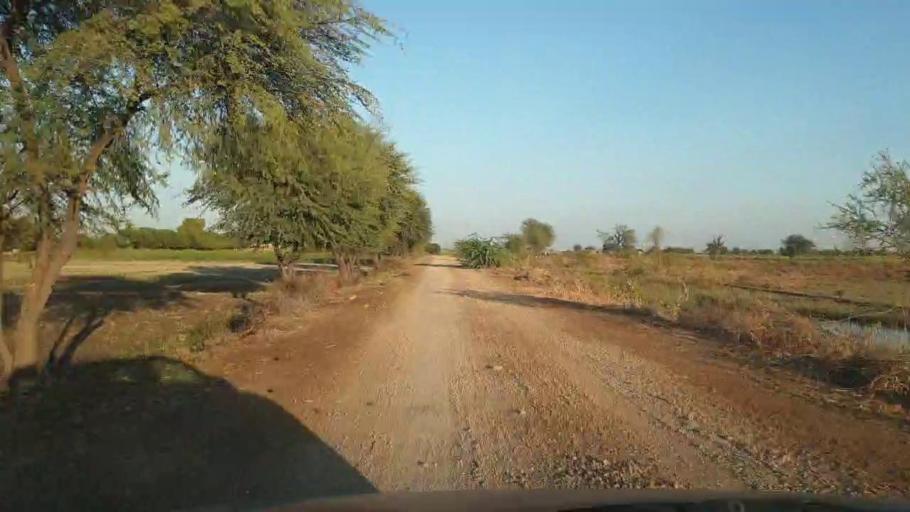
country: PK
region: Sindh
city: Dhoro Naro
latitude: 25.3596
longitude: 69.5695
